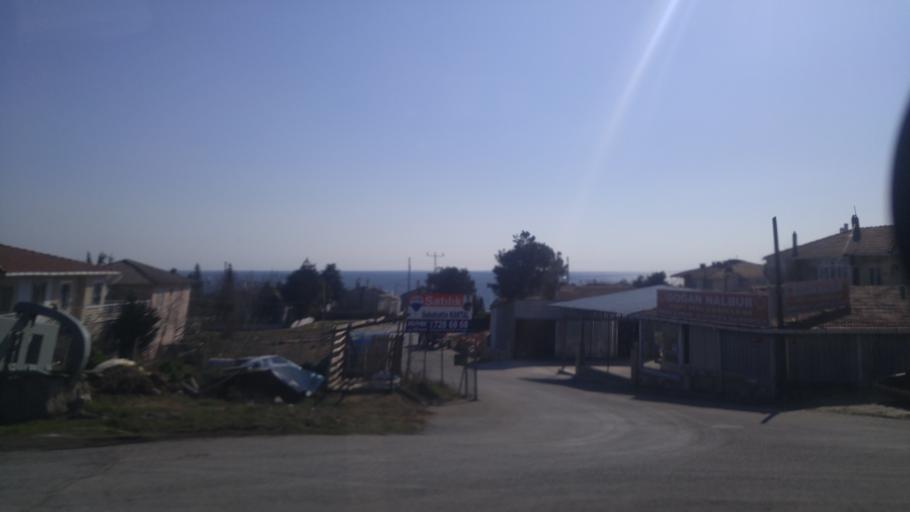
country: TR
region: Istanbul
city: Silivri
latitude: 41.0763
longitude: 28.1650
